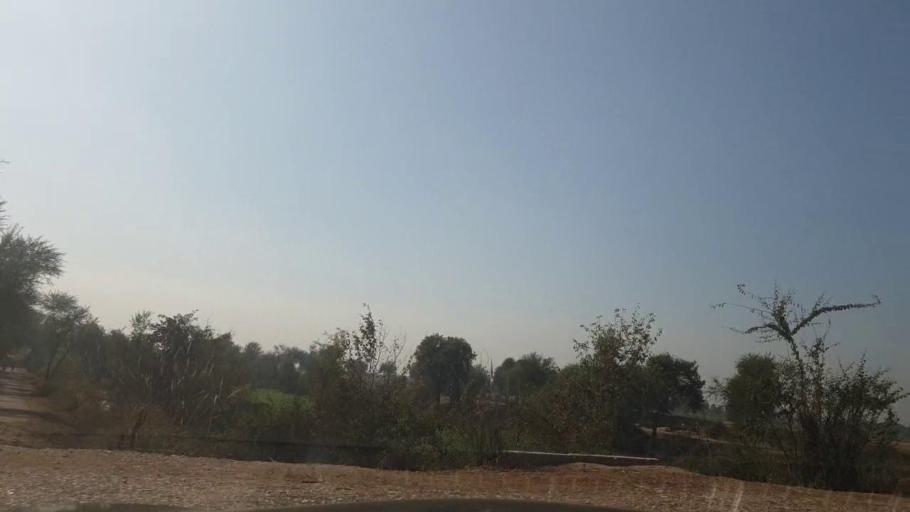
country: PK
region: Sindh
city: Ubauro
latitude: 28.1368
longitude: 69.6828
